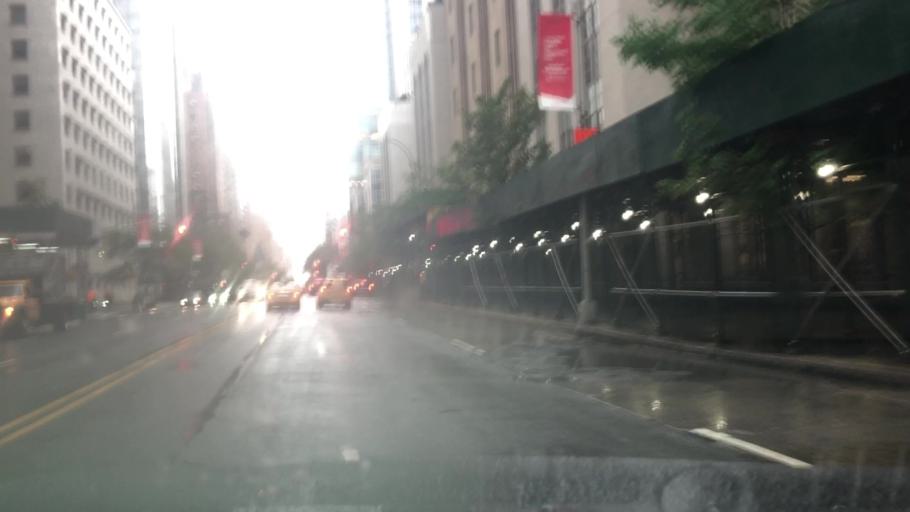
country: US
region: New York
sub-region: Queens County
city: Long Island City
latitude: 40.7645
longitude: -73.9555
